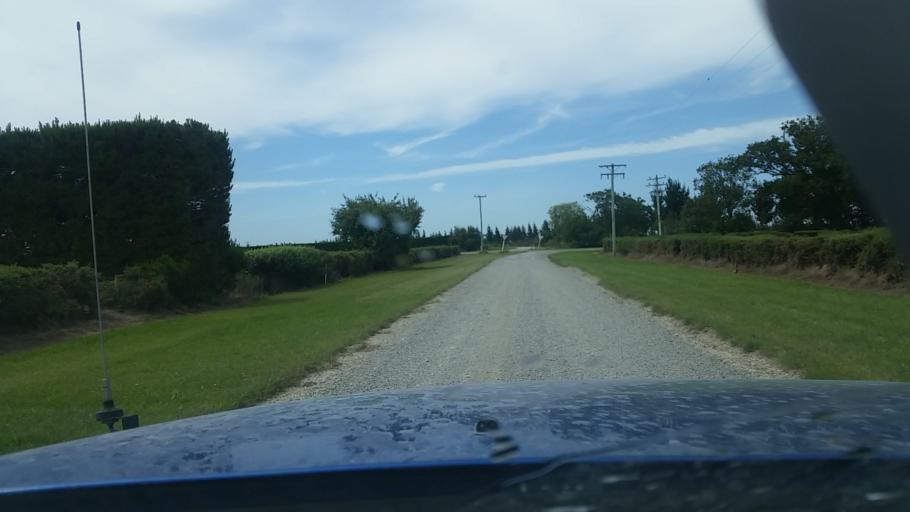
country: NZ
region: Canterbury
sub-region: Ashburton District
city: Tinwald
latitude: -44.0367
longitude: 171.7824
